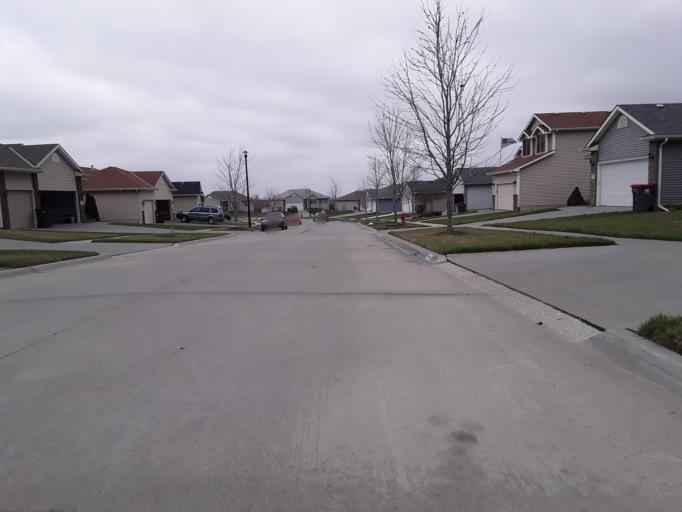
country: US
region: Nebraska
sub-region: Lancaster County
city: Lincoln
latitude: 40.8443
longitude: -96.5985
